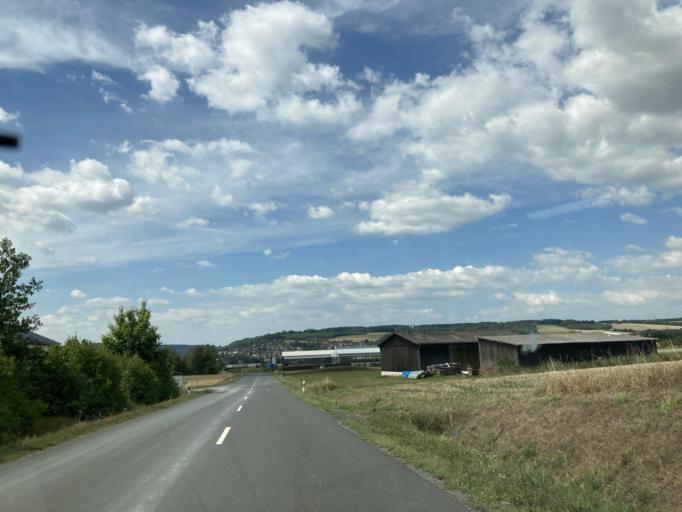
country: DE
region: Bavaria
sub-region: Upper Franconia
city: Kupferberg
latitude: 50.1409
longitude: 11.5474
